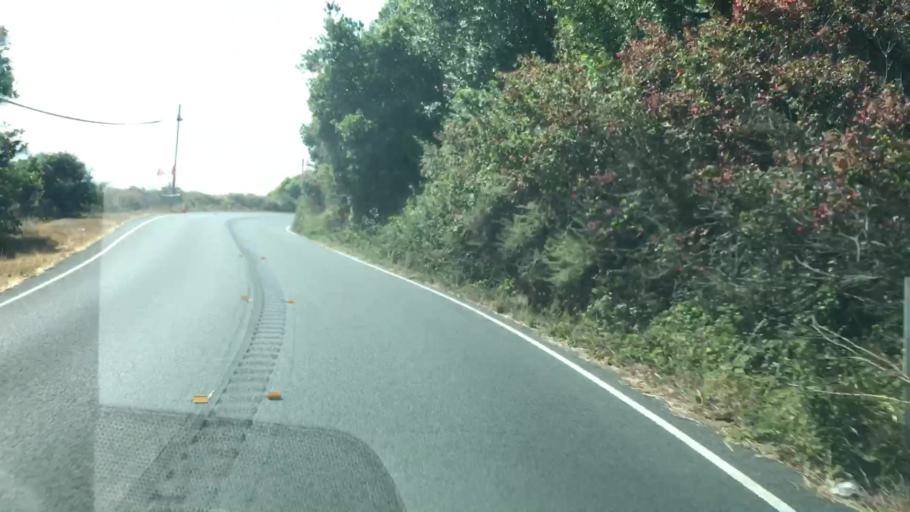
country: US
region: California
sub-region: Marin County
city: Inverness
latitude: 38.1006
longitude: -122.8350
